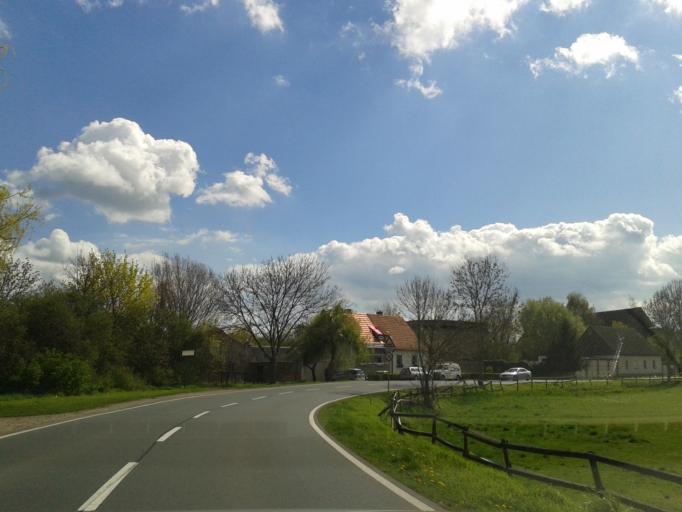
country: DE
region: Saxony-Anhalt
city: Wansleben
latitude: 51.4317
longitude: 11.7608
